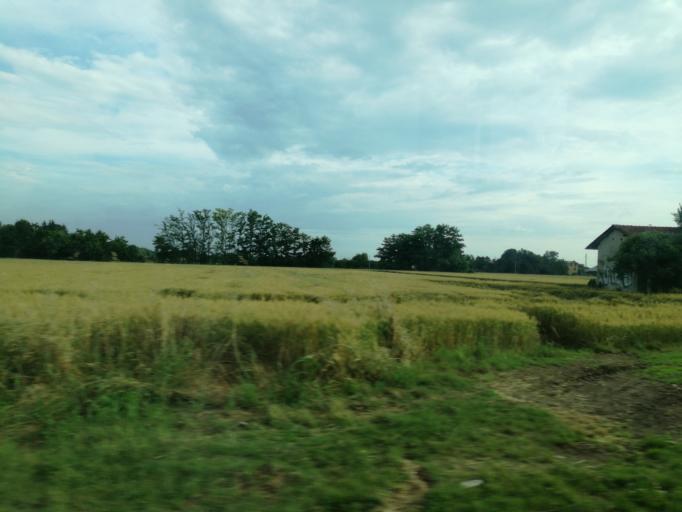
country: IT
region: Lombardy
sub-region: Provincia di Monza e Brianza
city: Velasca
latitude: 45.6214
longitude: 9.3446
